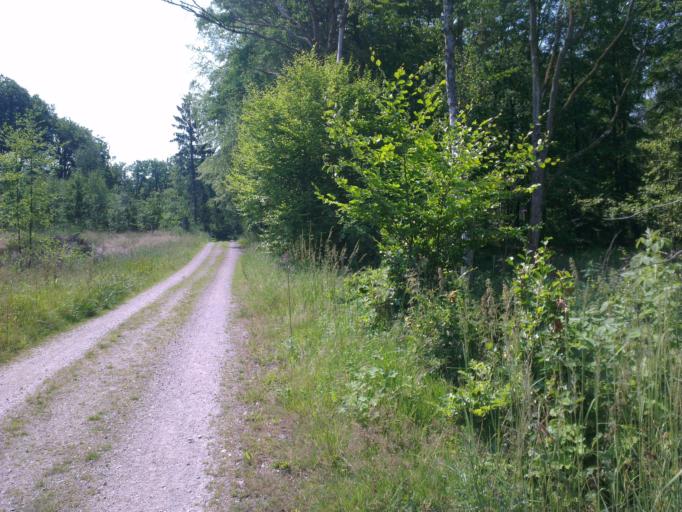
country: DK
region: Capital Region
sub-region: Allerod Kommune
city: Lillerod
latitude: 55.9267
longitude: 12.3623
